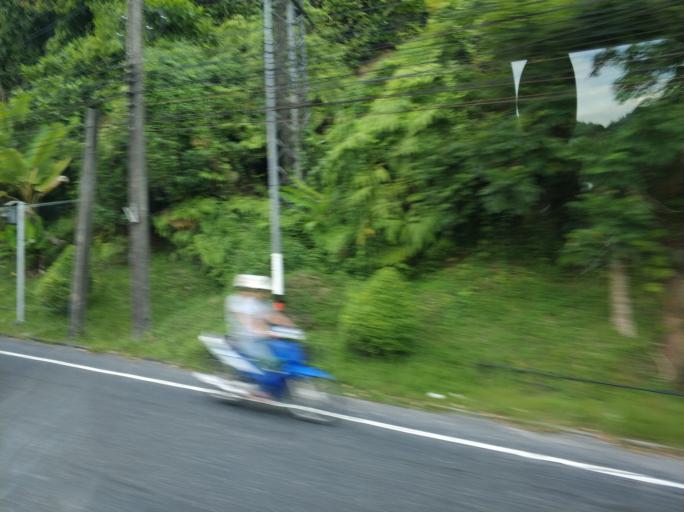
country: TH
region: Phuket
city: Kathu
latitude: 7.9034
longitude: 98.3222
